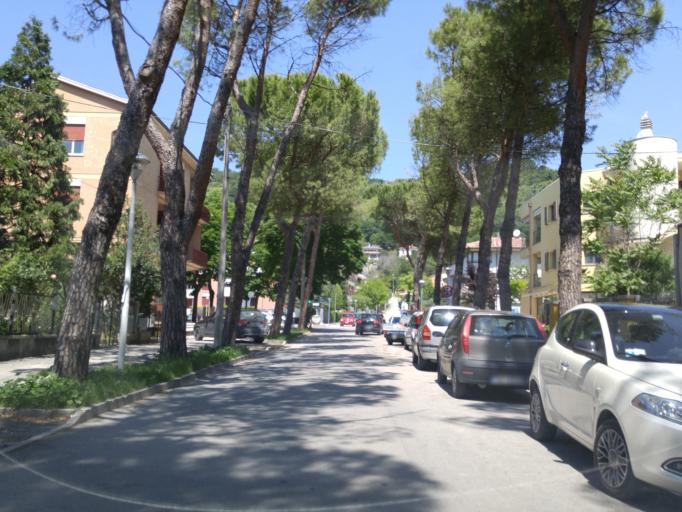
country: IT
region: The Marches
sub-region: Provincia di Pesaro e Urbino
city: Fossombrone
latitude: 43.6910
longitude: 12.8157
